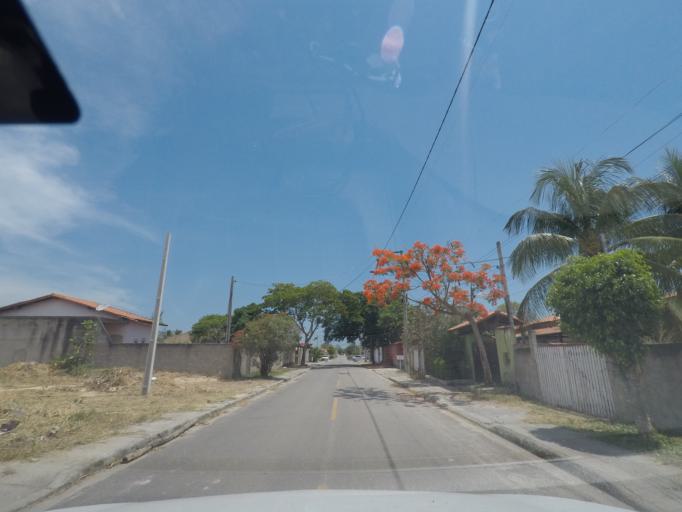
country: BR
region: Rio de Janeiro
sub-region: Niteroi
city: Niteroi
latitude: -22.9601
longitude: -42.9694
